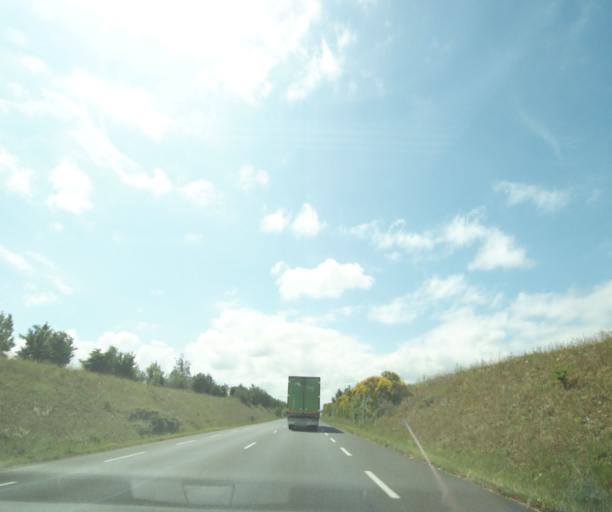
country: FR
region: Poitou-Charentes
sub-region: Departement des Deux-Sevres
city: Louzy
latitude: 47.0040
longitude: -0.1943
